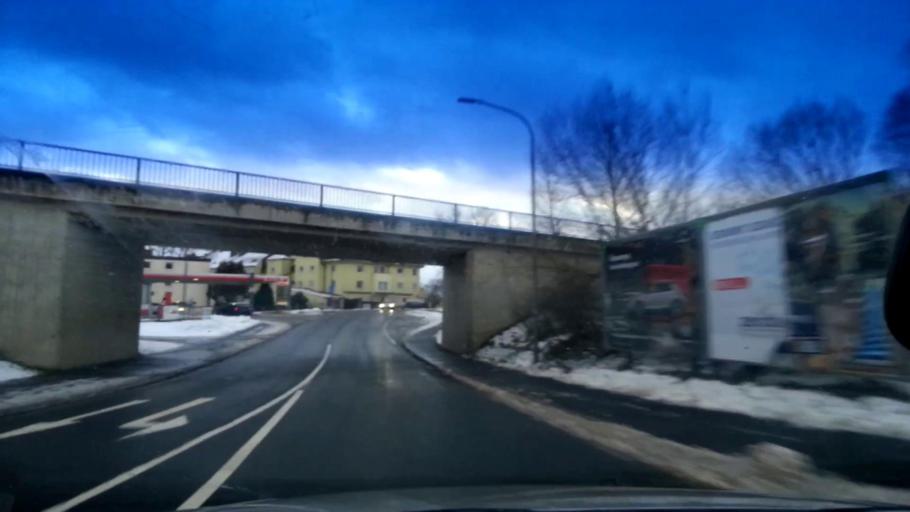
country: DE
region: Bavaria
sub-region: Upper Franconia
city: Selb
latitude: 50.1747
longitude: 12.1279
